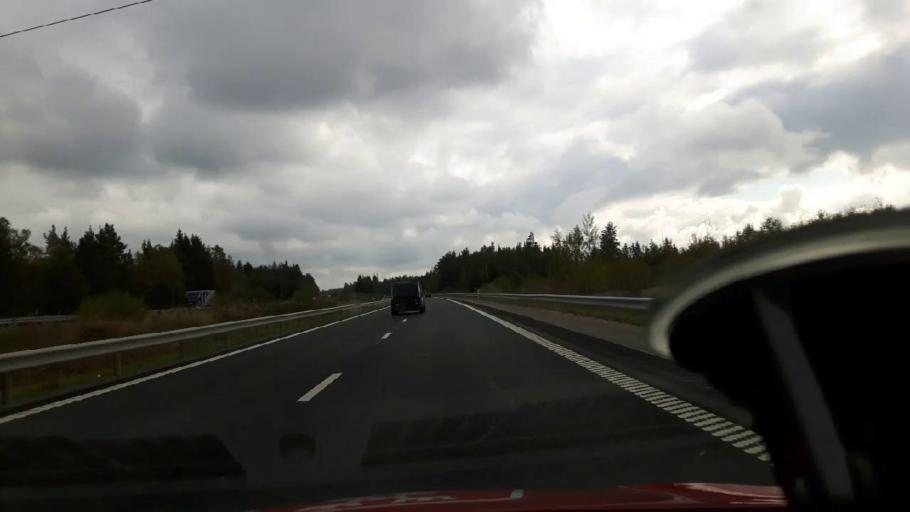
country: SE
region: Gaevleborg
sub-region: Gavle Kommun
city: Gavle
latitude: 60.6262
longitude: 17.1542
